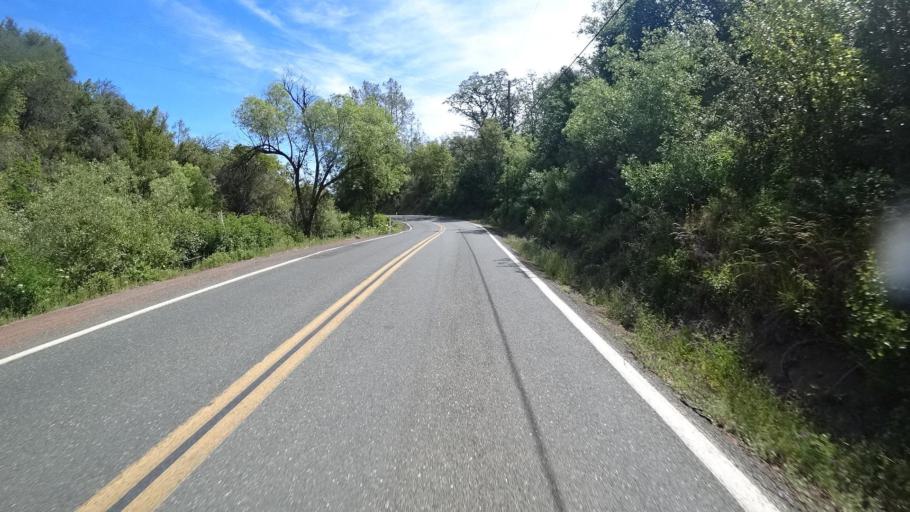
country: US
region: California
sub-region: Lake County
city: Lower Lake
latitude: 38.8942
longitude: -122.6531
